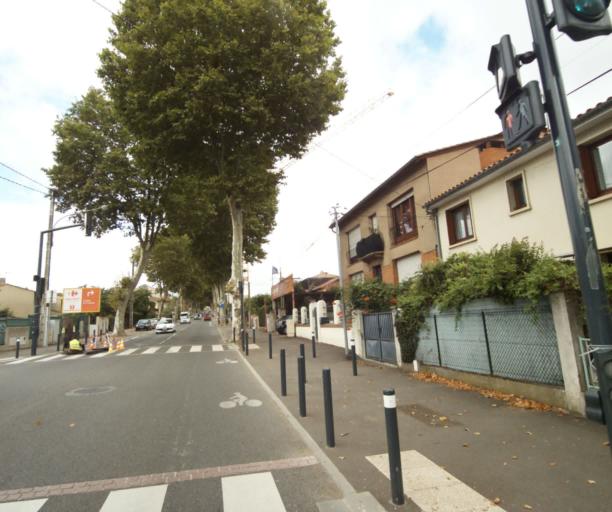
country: FR
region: Midi-Pyrenees
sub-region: Departement de la Haute-Garonne
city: Balma
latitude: 43.5948
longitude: 1.4884
